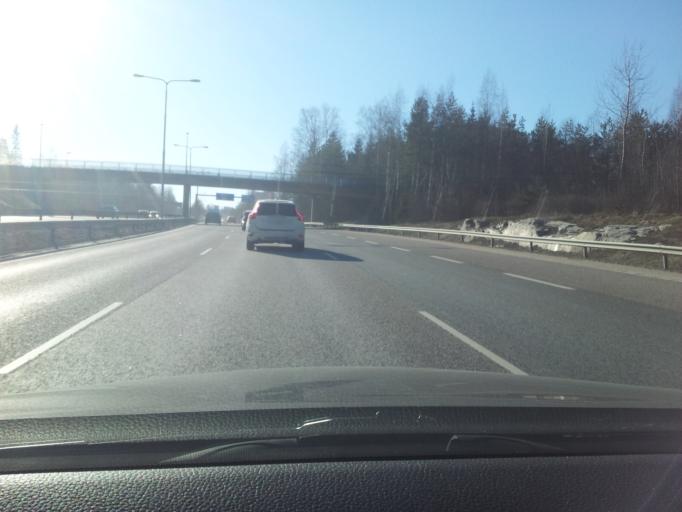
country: FI
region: Uusimaa
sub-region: Helsinki
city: Helsinki
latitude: 60.2385
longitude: 24.9112
